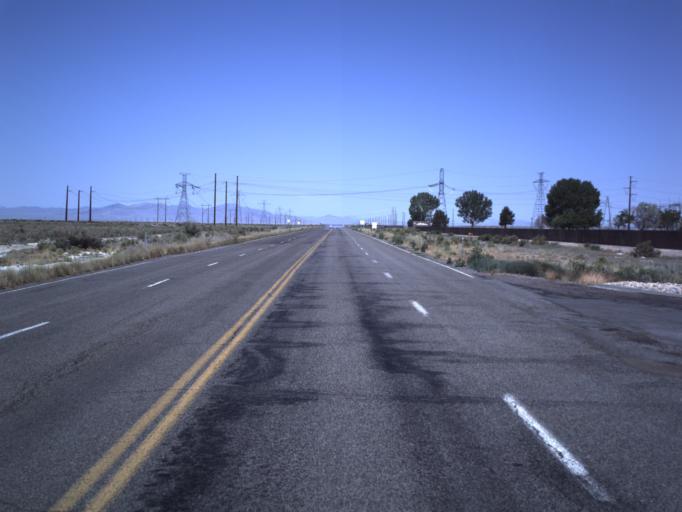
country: US
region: Utah
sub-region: Millard County
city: Delta
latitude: 39.4941
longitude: -112.5739
